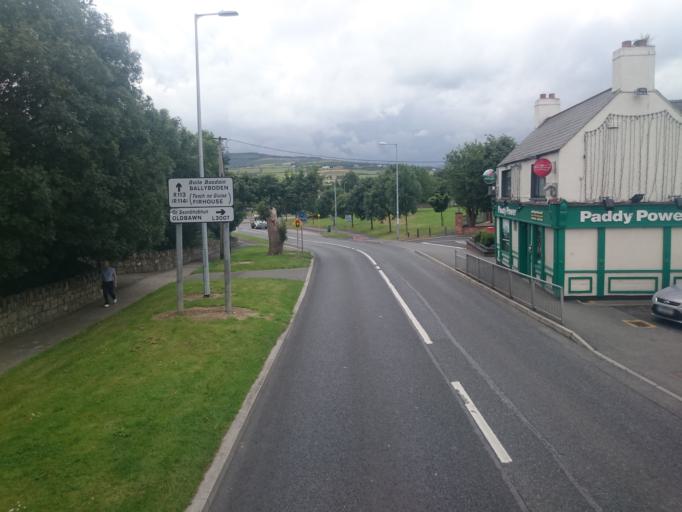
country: IE
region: Leinster
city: Oldbawn
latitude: 53.2782
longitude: -6.3580
